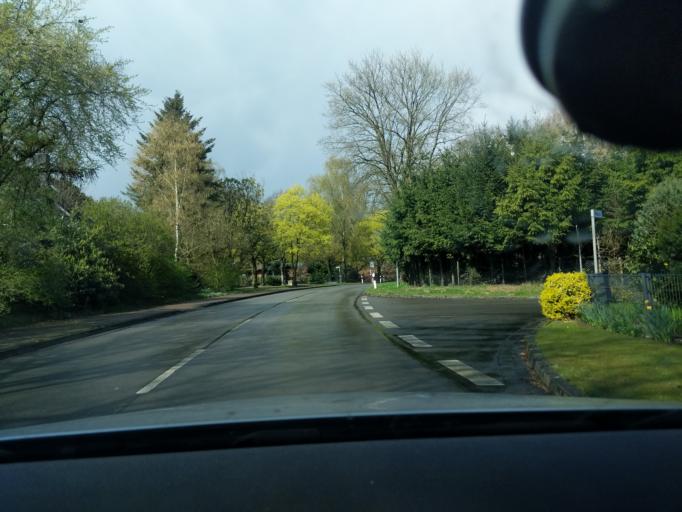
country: DE
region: Lower Saxony
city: Bargstedt
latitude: 53.4557
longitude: 9.4530
